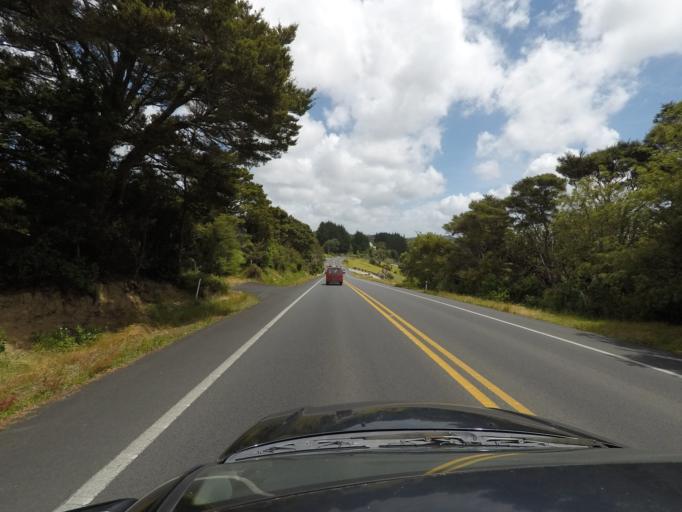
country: NZ
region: Auckland
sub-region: Auckland
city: Warkworth
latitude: -36.5338
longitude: 174.6875
